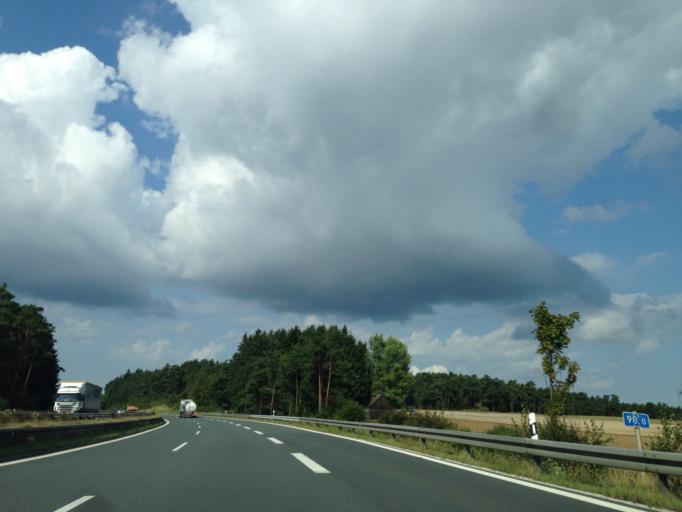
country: DE
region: Bavaria
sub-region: Upper Franconia
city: Kasendorf
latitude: 50.0119
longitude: 11.3215
